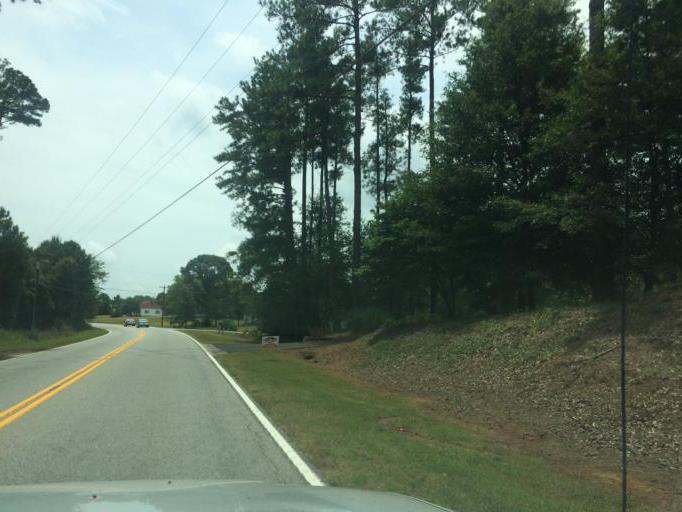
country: US
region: South Carolina
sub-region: Anderson County
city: Centerville
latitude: 34.5339
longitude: -82.8034
